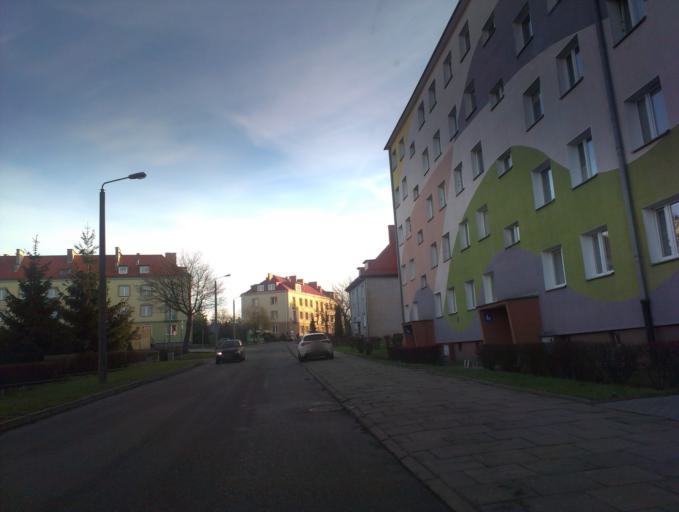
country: PL
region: West Pomeranian Voivodeship
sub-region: Powiat szczecinecki
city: Szczecinek
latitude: 53.6997
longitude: 16.7015
